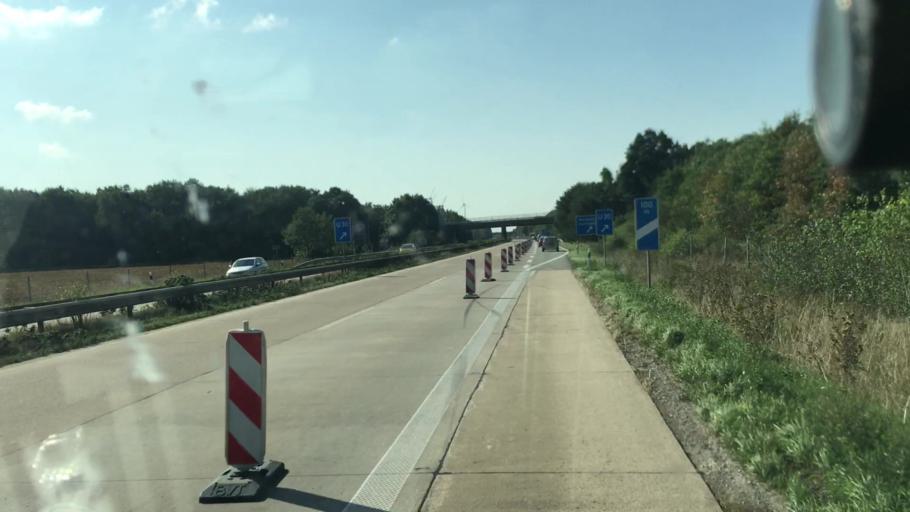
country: DE
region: Lower Saxony
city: Wardenburg
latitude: 53.0345
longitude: 8.2170
